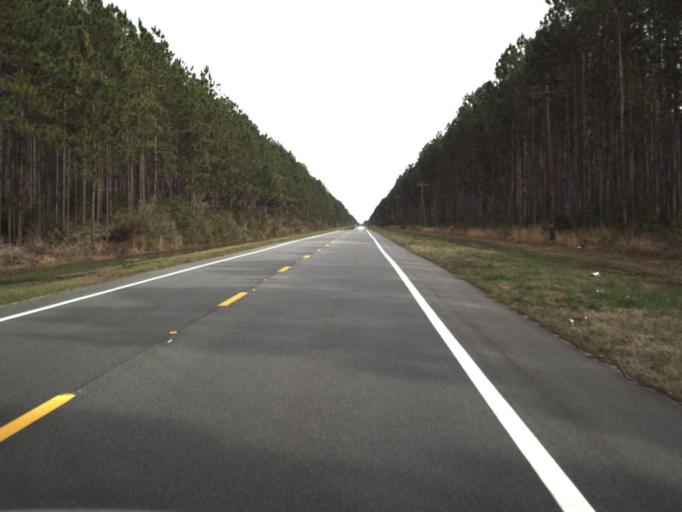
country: US
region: Florida
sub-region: Bay County
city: Callaway
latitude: 30.1455
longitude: -85.4405
